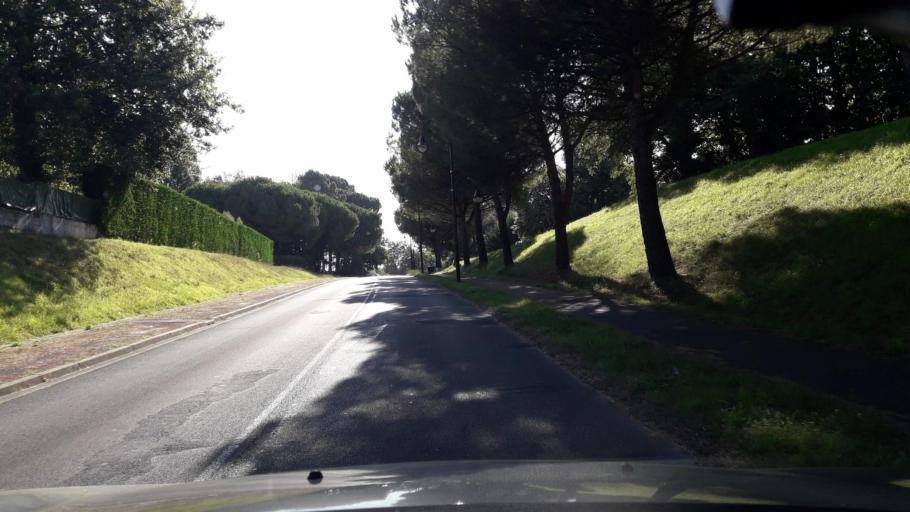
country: FR
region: Poitou-Charentes
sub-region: Departement de la Charente-Maritime
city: Les Mathes
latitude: 45.7149
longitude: -1.1463
